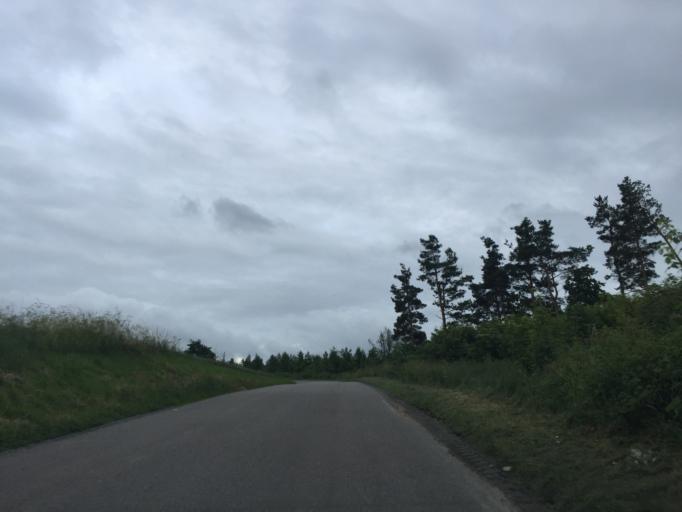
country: DK
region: Central Jutland
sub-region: Silkeborg Kommune
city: Silkeborg
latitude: 56.2441
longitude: 9.5335
